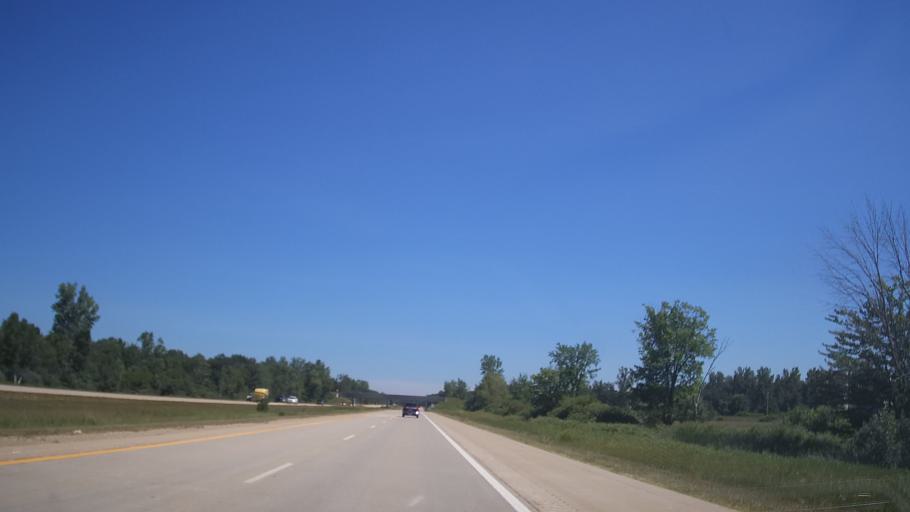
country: US
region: Michigan
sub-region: Midland County
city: Coleman
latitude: 43.7596
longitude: -84.5549
